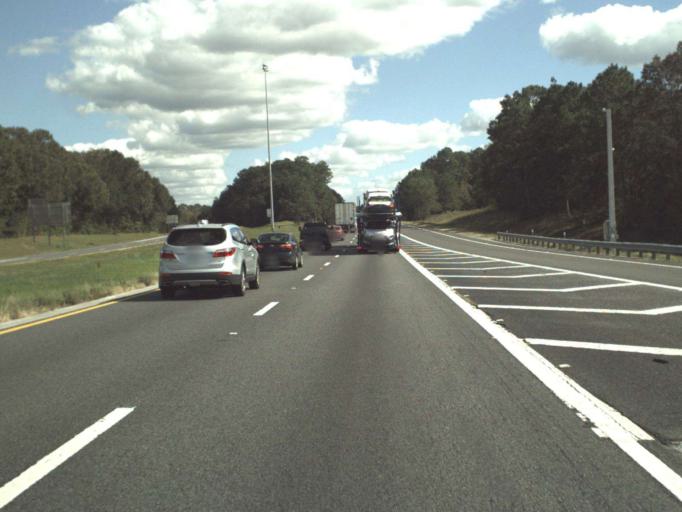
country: US
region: Florida
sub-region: Jackson County
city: Sneads
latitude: 30.6549
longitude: -85.0343
